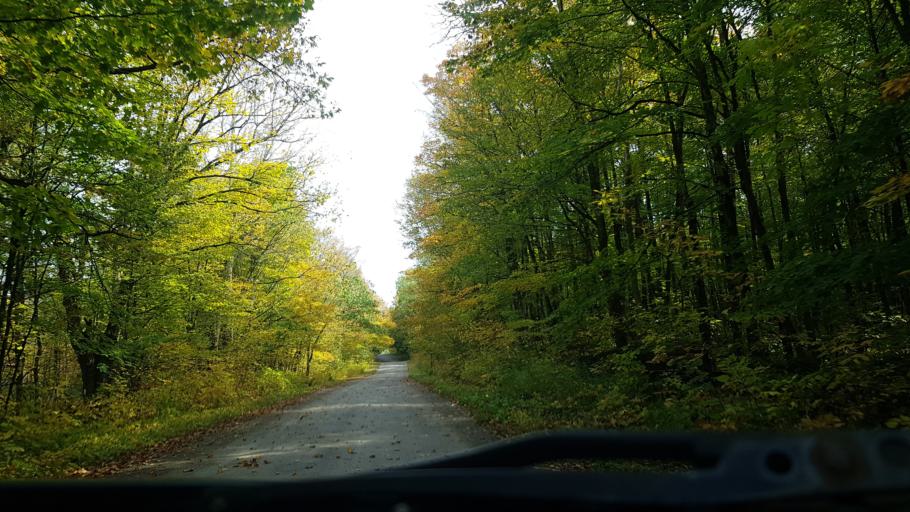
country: CA
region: Ontario
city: Orillia
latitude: 44.6759
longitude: -79.0878
